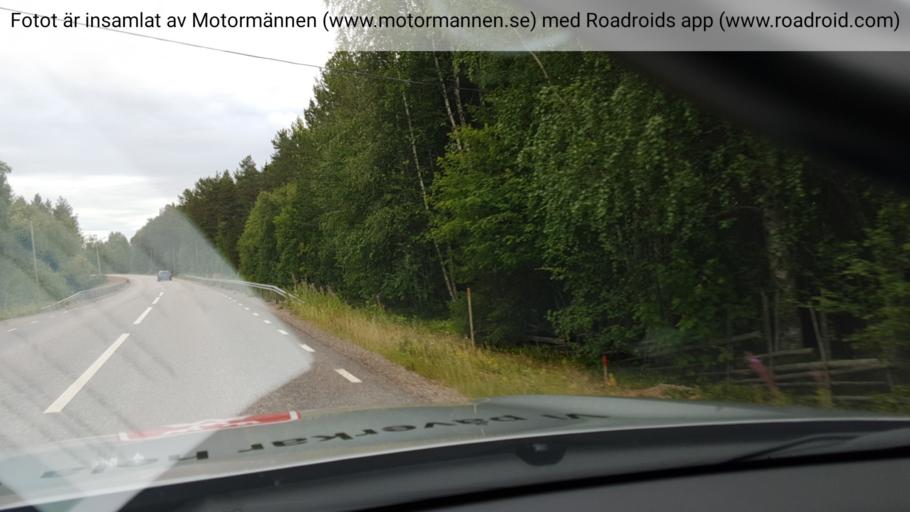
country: SE
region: Norrbotten
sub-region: Overkalix Kommun
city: OEverkalix
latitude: 66.5103
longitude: 22.7654
